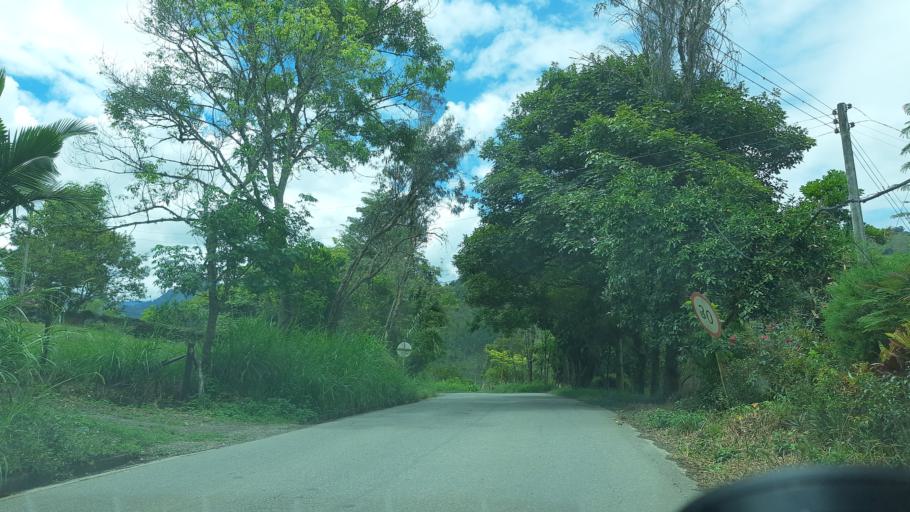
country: CO
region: Cundinamarca
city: Tenza
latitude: 5.0389
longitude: -73.3887
